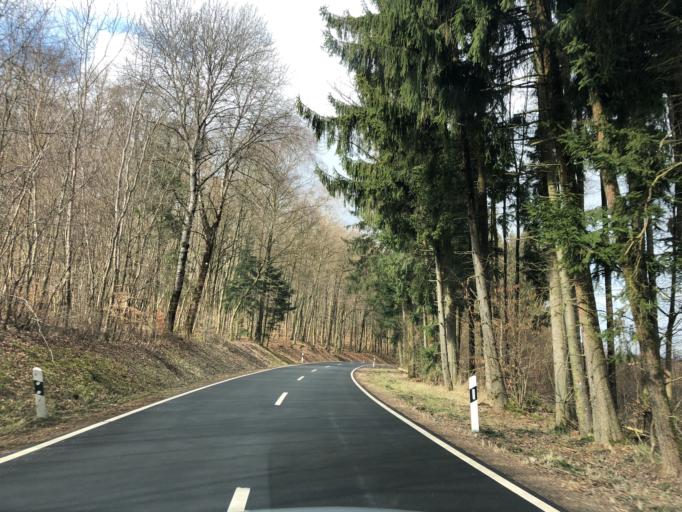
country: DE
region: Hesse
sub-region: Regierungsbezirk Giessen
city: Schotten
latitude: 50.4935
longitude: 9.0704
